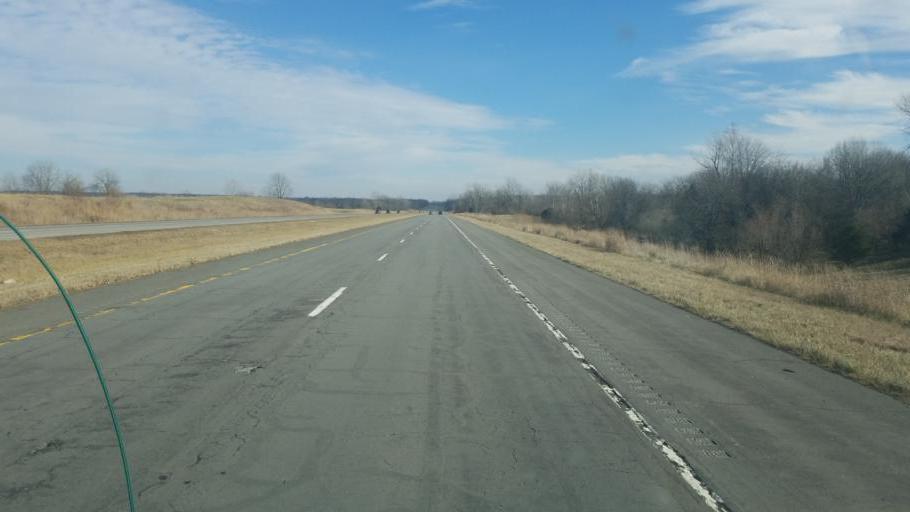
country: US
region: Illinois
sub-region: Saline County
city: Carrier Mills
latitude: 37.7303
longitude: -88.7730
